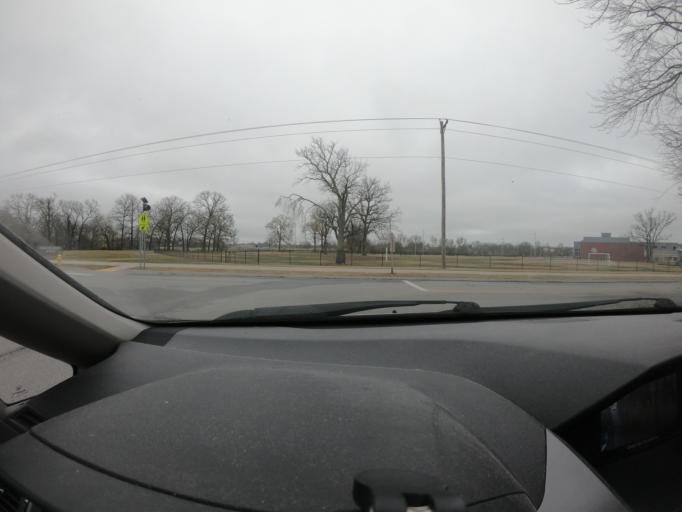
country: US
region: Arkansas
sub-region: Benton County
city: Bentonville
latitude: 36.3434
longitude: -94.2402
